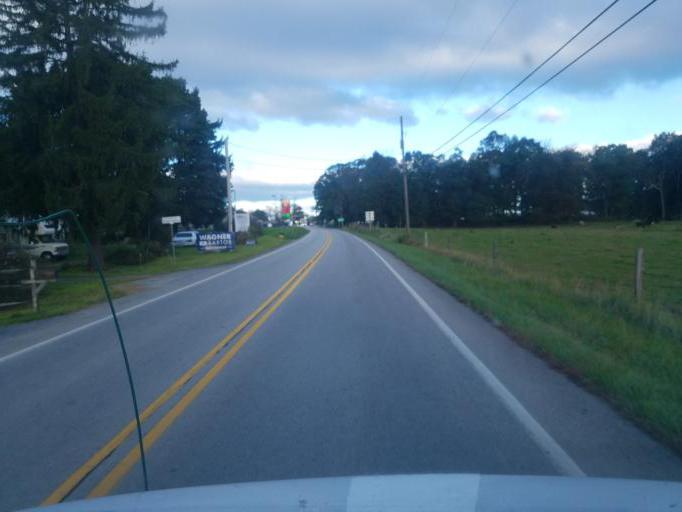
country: US
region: Pennsylvania
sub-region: Adams County
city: Lake Meade
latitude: 39.9383
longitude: -77.0596
